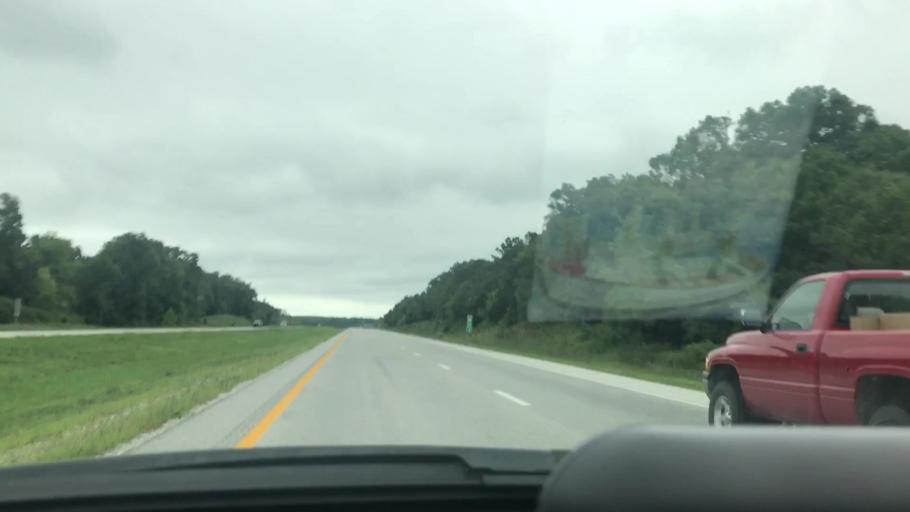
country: US
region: Missouri
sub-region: Greene County
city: Strafford
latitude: 37.2842
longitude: -93.1961
